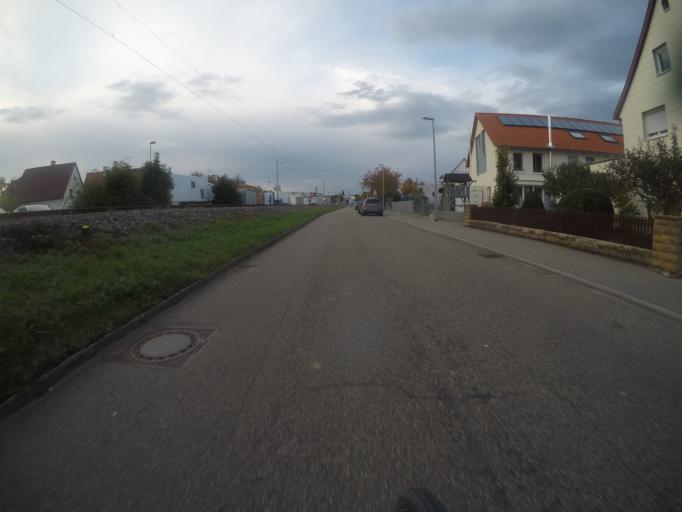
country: DE
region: Baden-Wuerttemberg
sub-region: Regierungsbezirk Stuttgart
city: Holzgerlingen
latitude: 48.6353
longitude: 9.0083
